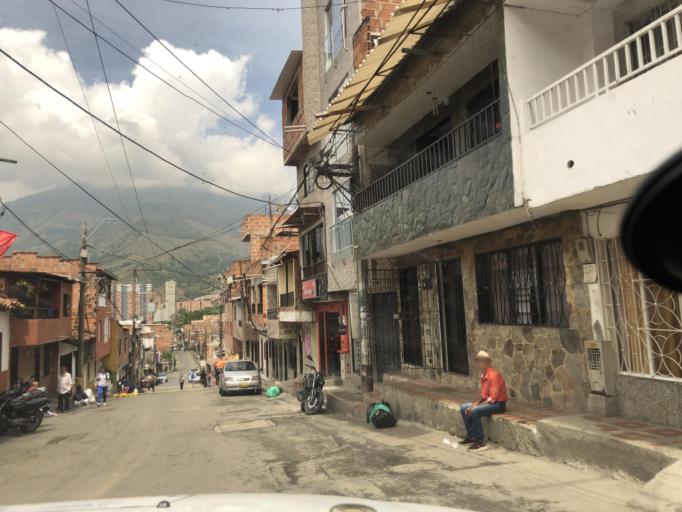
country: CO
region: Antioquia
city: Bello
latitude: 6.3314
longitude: -75.5362
